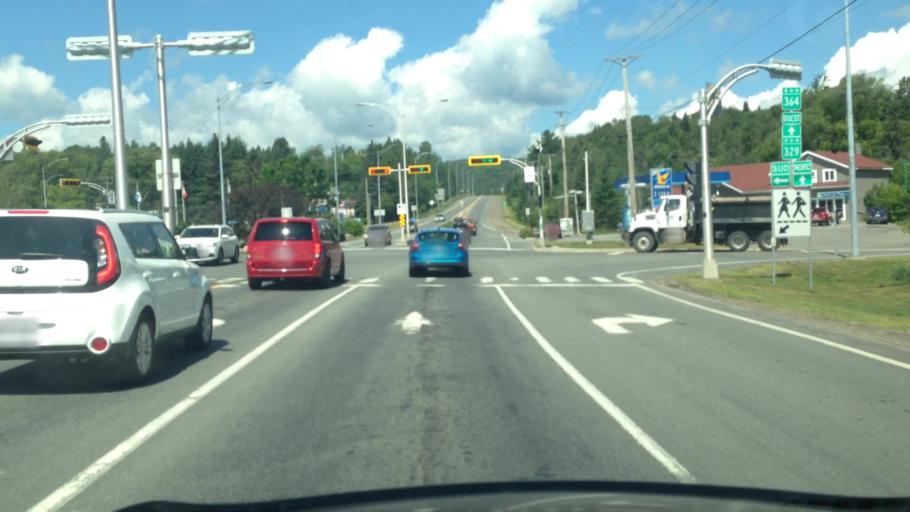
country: CA
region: Quebec
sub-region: Laurentides
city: Saint-Sauveur
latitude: 45.9036
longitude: -74.2451
